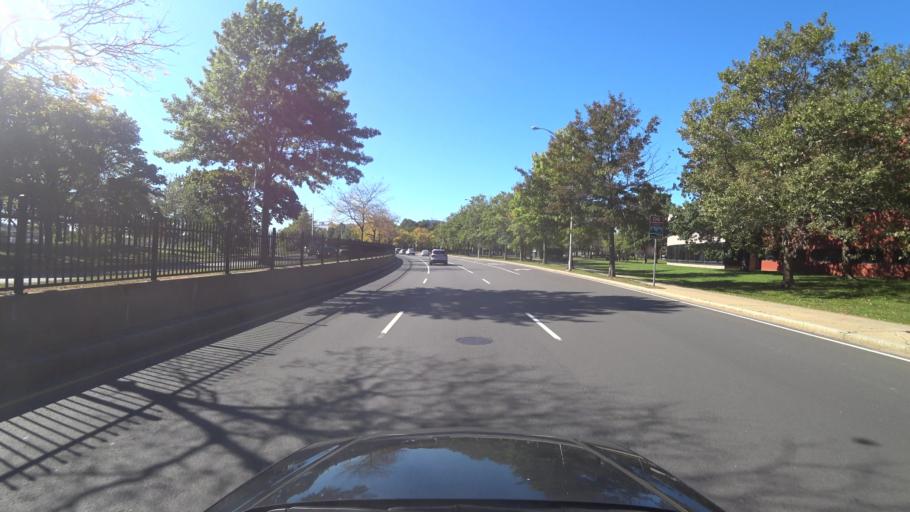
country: US
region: Massachusetts
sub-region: Essex County
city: Lynn
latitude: 42.4600
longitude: -70.9437
